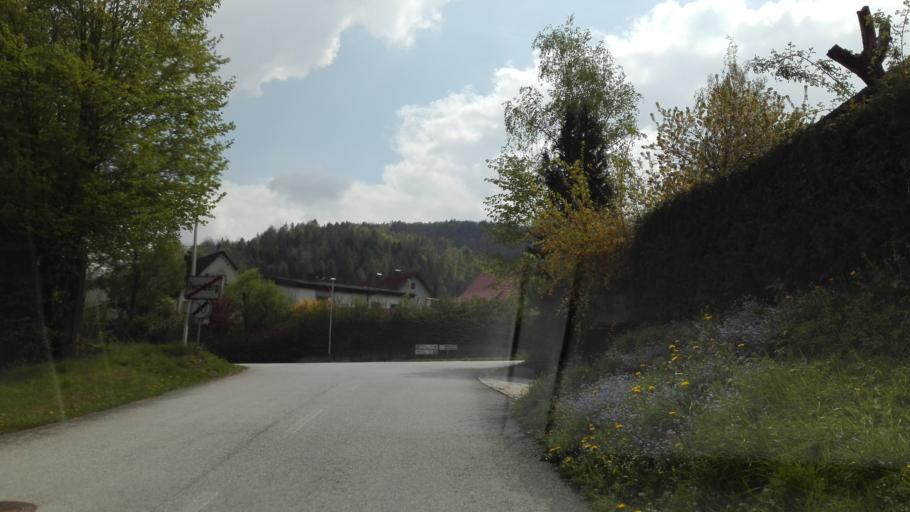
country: AT
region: Upper Austria
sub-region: Politischer Bezirk Steyr-Land
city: Ternberg
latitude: 47.9420
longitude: 14.3558
